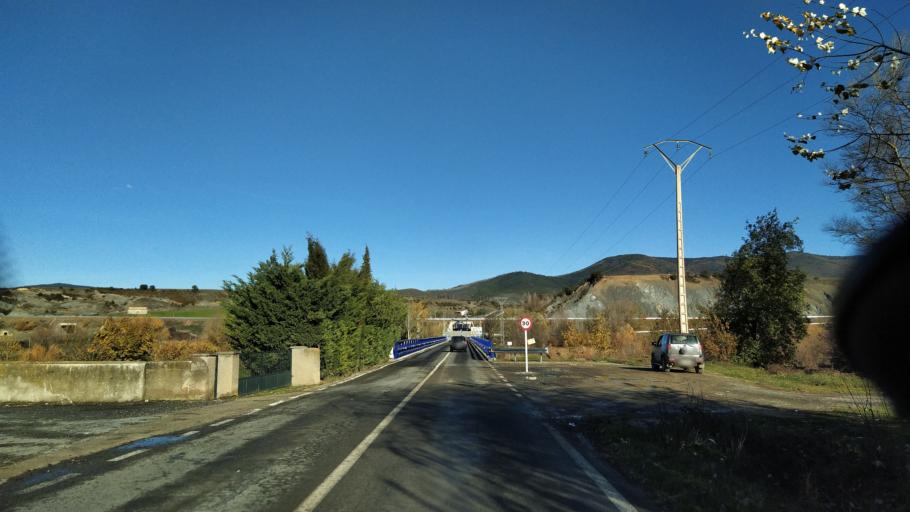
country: ES
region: Aragon
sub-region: Provincia de Huesca
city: Santa Cruz de la Seros
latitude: 42.5610
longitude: -0.7127
